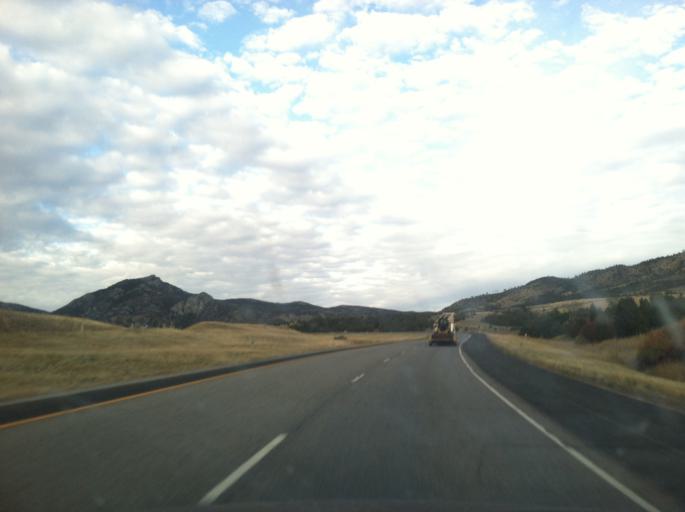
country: US
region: Montana
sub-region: Jefferson County
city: Whitehall
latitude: 45.8740
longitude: -111.9326
